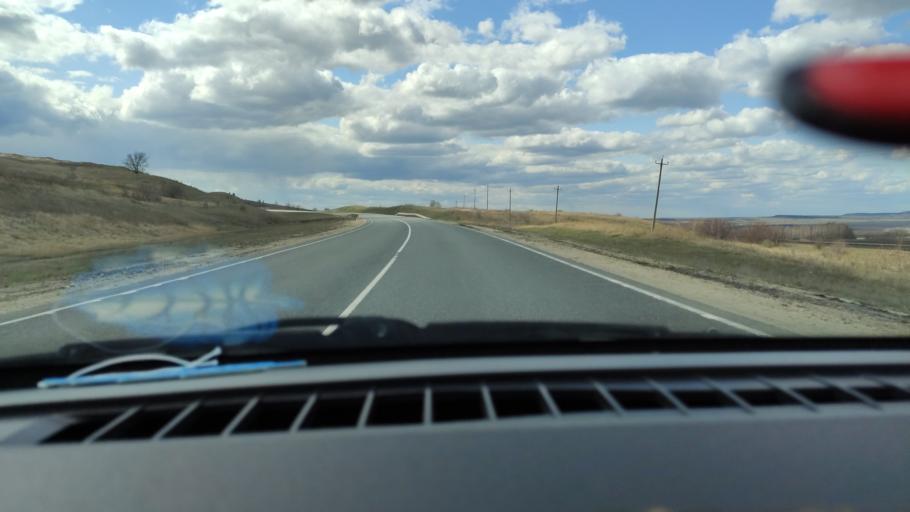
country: RU
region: Saratov
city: Alekseyevka
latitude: 52.3261
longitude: 47.9203
